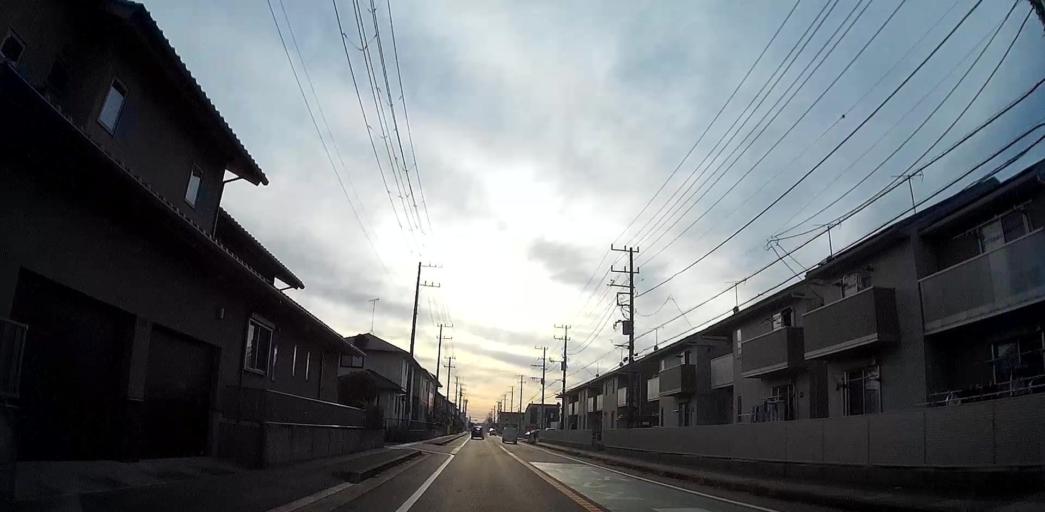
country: JP
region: Chiba
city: Hasaki
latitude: 35.7954
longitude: 140.7751
